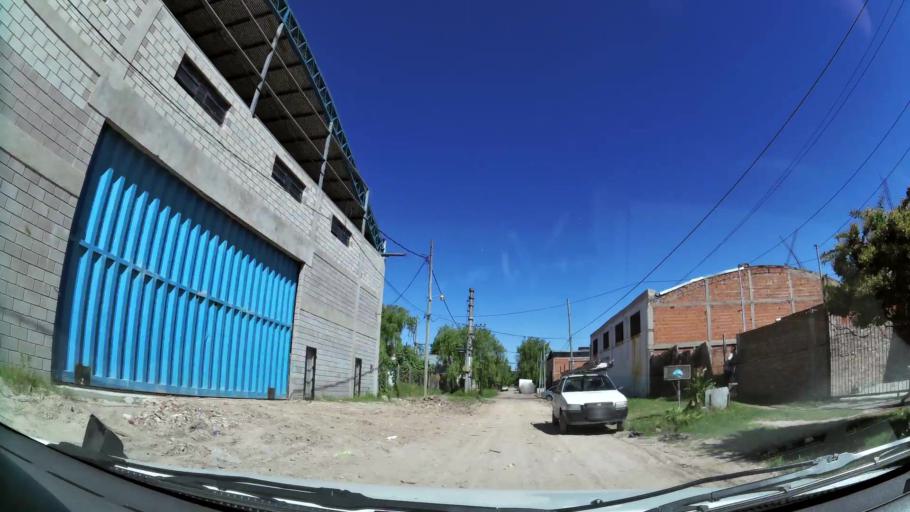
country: AR
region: Buenos Aires
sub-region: Partido de General San Martin
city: General San Martin
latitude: -34.5155
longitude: -58.5843
